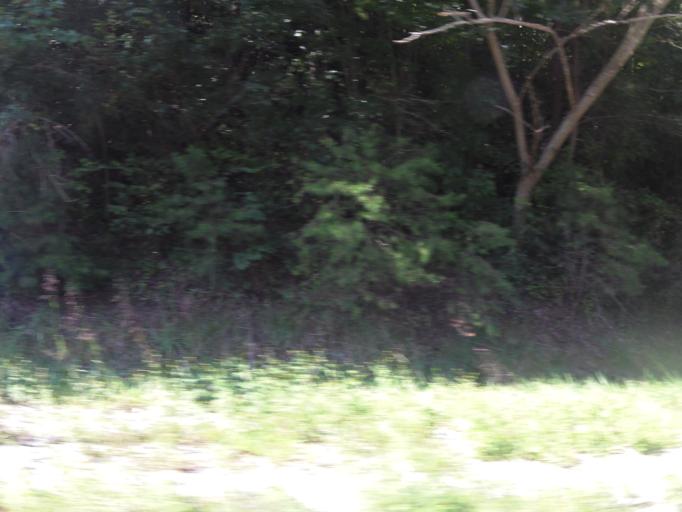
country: US
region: Kentucky
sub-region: Bell County
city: Pineville
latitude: 36.7365
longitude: -83.6054
